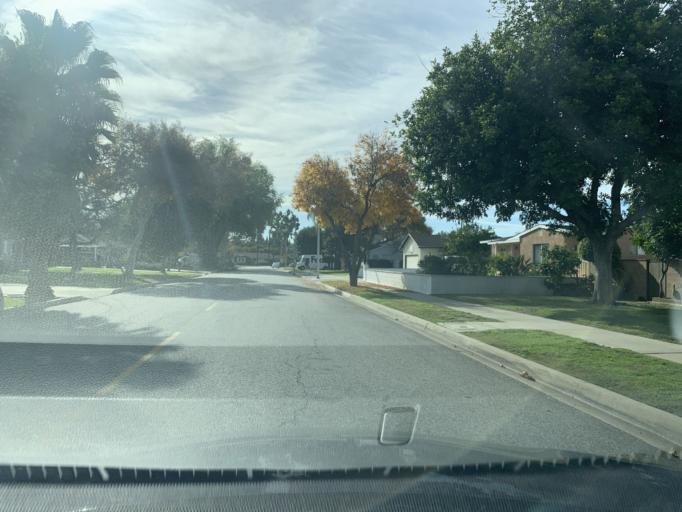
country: US
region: California
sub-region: Los Angeles County
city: West Covina
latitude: 34.0765
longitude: -117.9391
